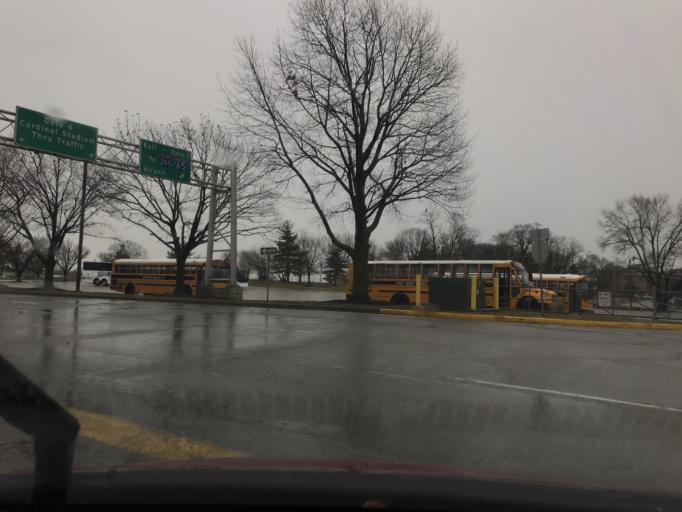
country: US
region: Kentucky
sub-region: Jefferson County
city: Audubon Park
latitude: 38.1957
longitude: -85.7419
